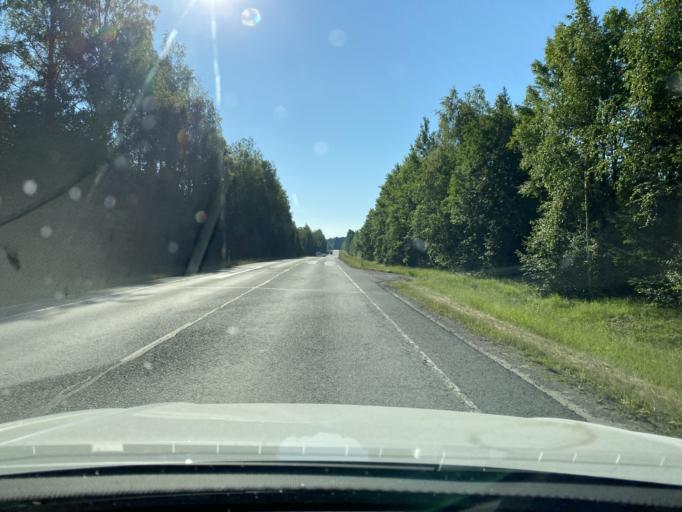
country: FI
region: Haeme
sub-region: Forssa
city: Tammela
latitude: 60.8292
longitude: 23.8818
